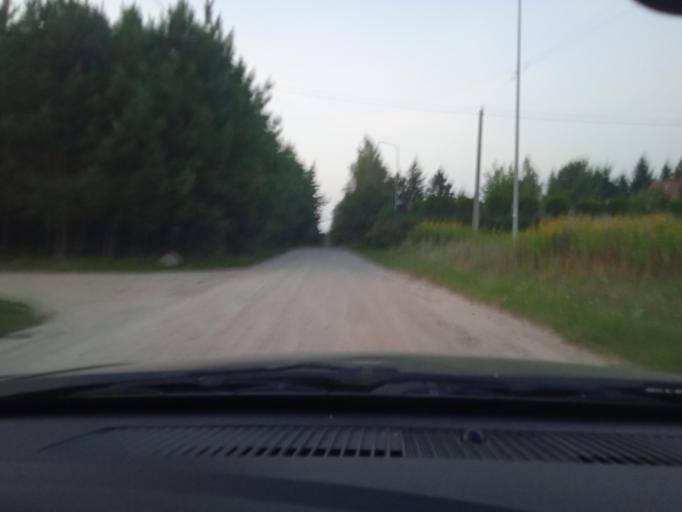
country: PL
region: Masovian Voivodeship
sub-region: Powiat nowodworski
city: Pomiechowek
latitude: 52.4880
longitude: 20.7036
